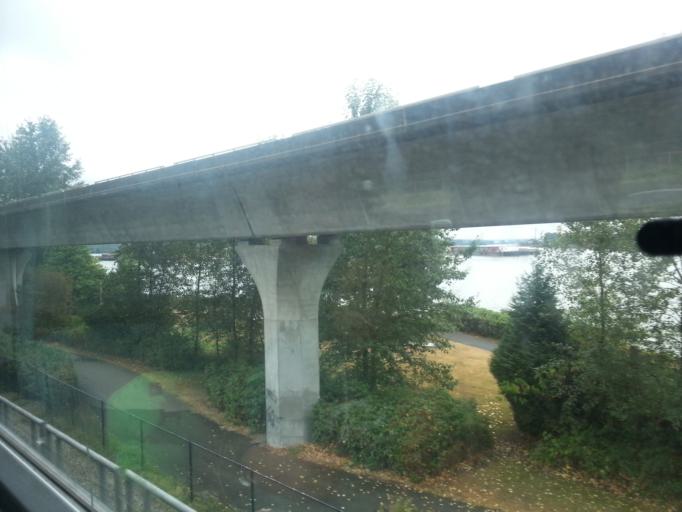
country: CA
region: British Columbia
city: New Westminster
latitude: 49.2136
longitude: -122.8948
